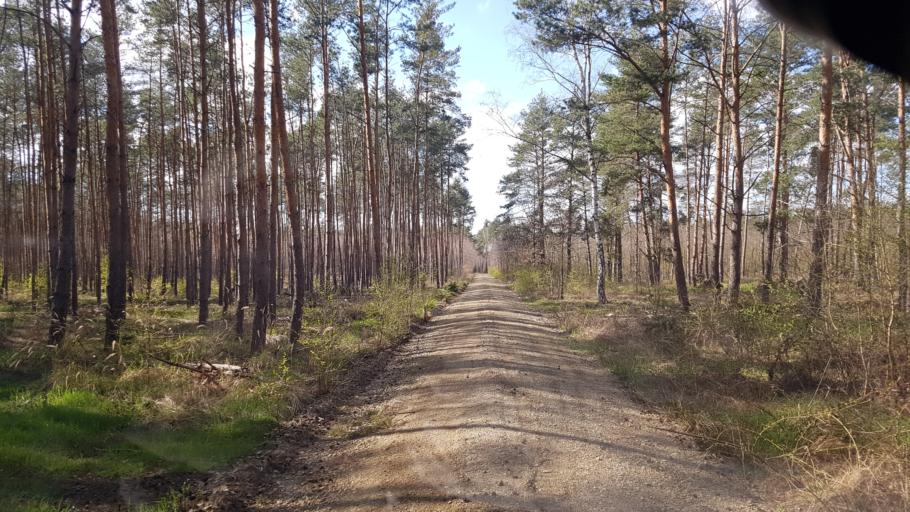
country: DE
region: Brandenburg
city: Muhlberg
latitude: 51.4802
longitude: 13.2862
